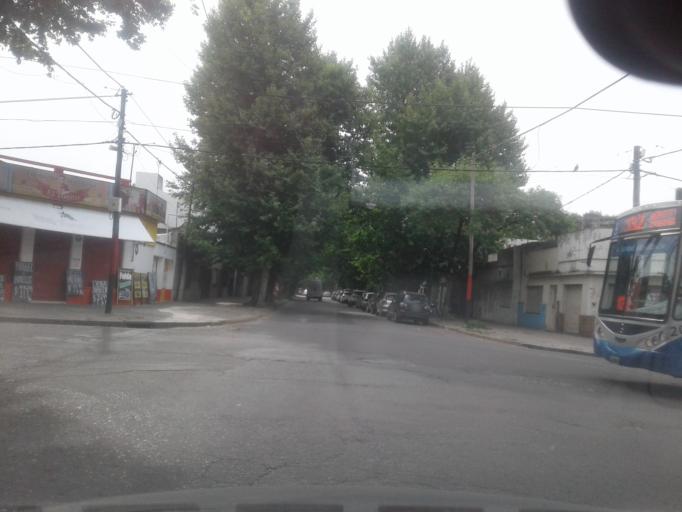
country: AR
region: Santa Fe
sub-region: Departamento de Rosario
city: Rosario
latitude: -32.9668
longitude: -60.6547
